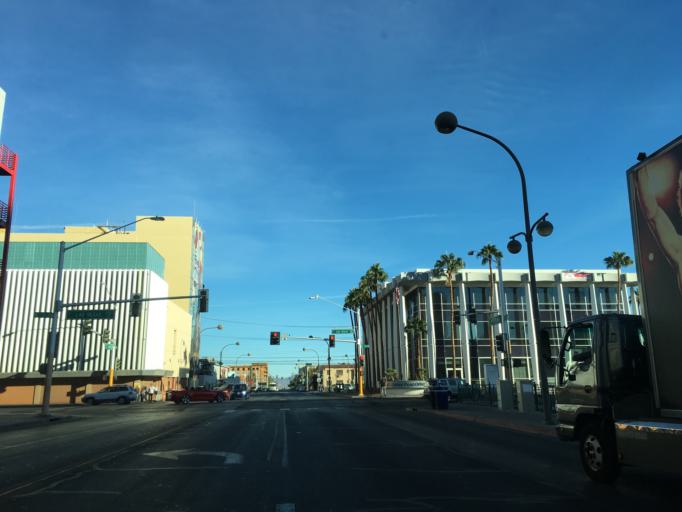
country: US
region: Nevada
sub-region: Clark County
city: Las Vegas
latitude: 36.1683
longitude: -115.1420
